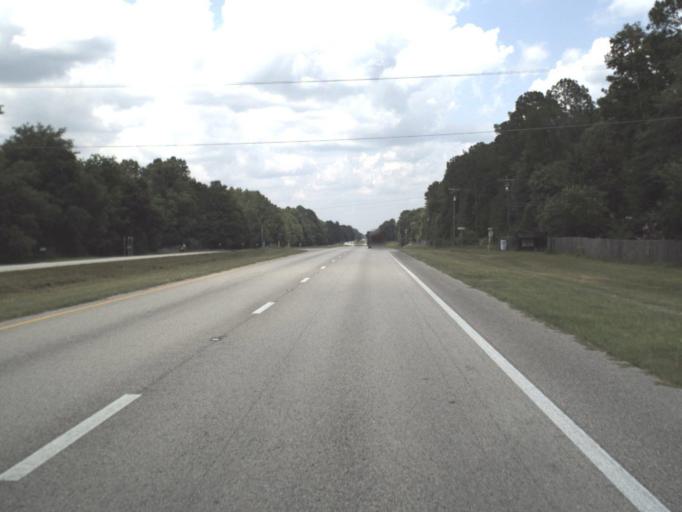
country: US
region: Florida
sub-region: Alachua County
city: Waldo
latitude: 29.7327
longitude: -82.2459
